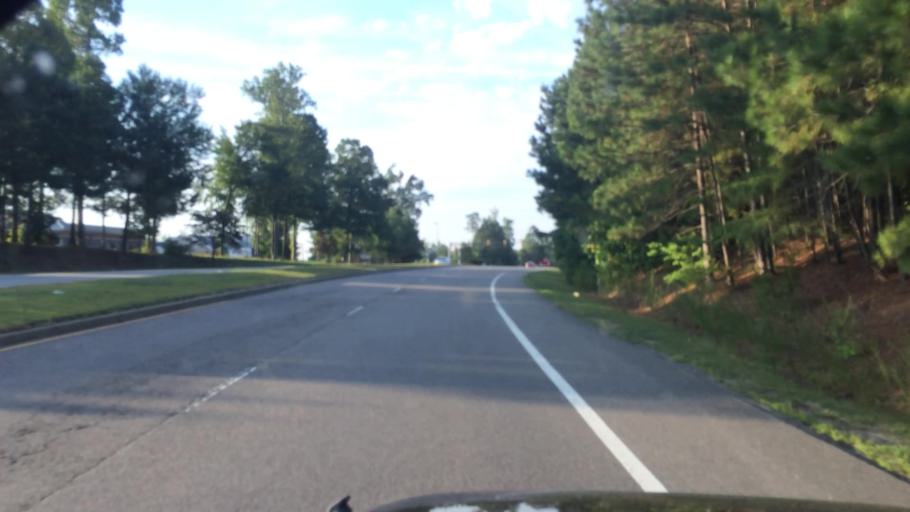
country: US
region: Virginia
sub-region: James City County
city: Williamsburg
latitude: 37.3411
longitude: -76.7392
